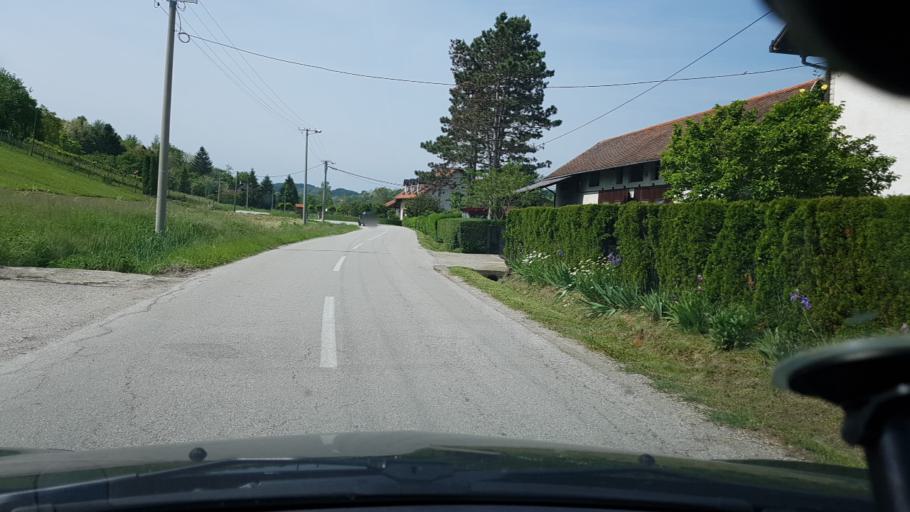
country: HR
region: Krapinsko-Zagorska
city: Marija Bistrica
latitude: 45.9341
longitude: 16.1983
